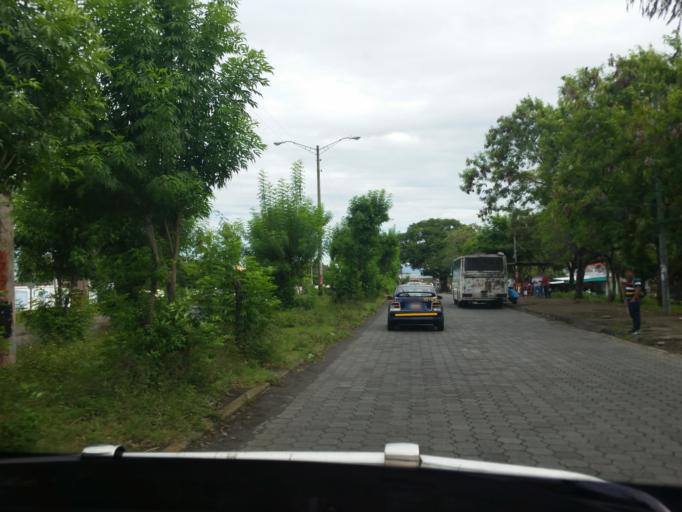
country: NI
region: Managua
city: Managua
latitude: 12.1352
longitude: -86.2291
